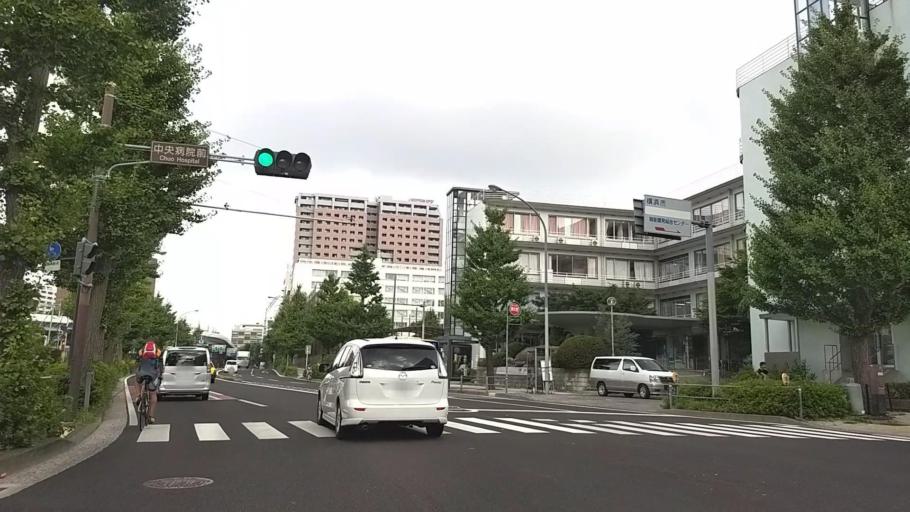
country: JP
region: Kanagawa
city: Yokohama
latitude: 35.4402
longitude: 139.6439
